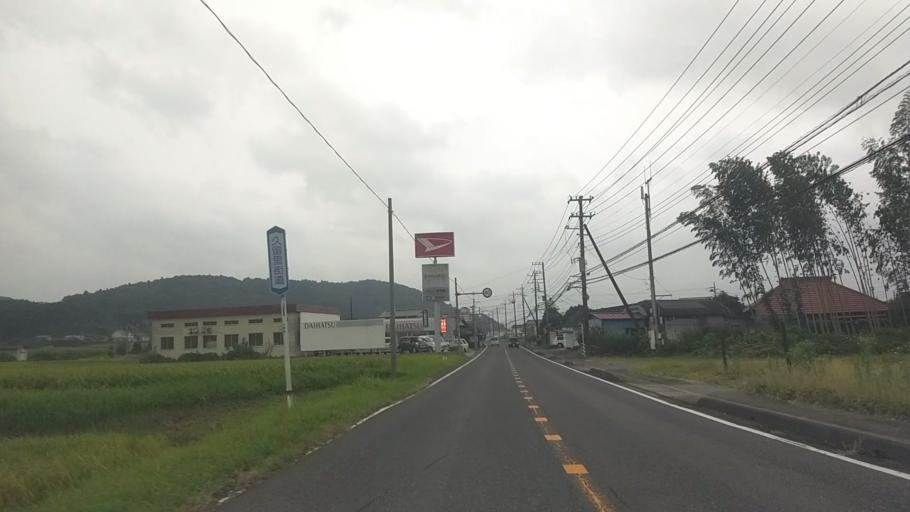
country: JP
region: Chiba
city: Kisarazu
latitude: 35.3103
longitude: 140.0650
